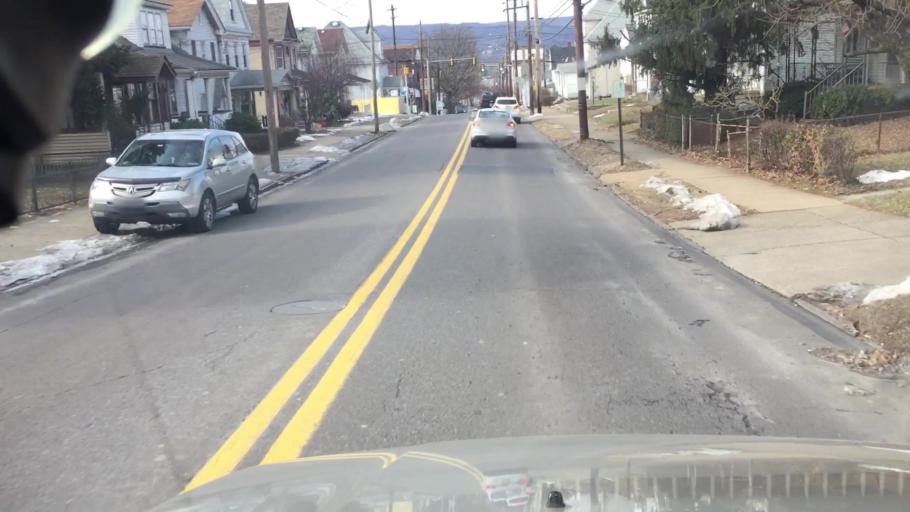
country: US
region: Pennsylvania
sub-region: Luzerne County
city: Ashley
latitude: 41.2299
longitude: -75.8987
